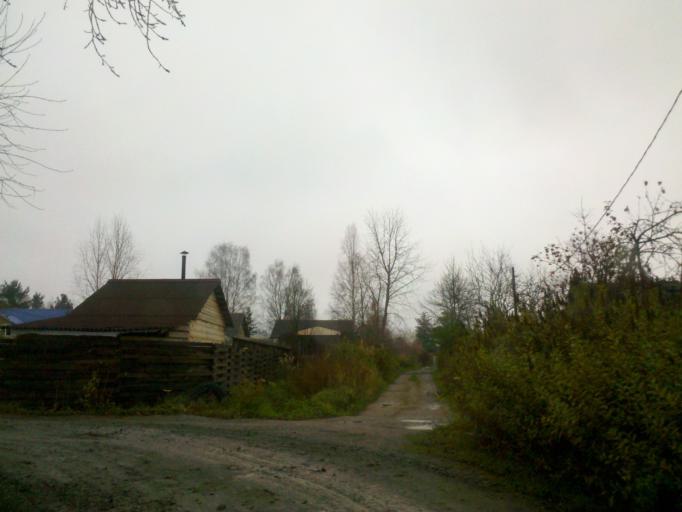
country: RU
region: Republic of Karelia
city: Shuya
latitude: 61.8541
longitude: 34.1476
